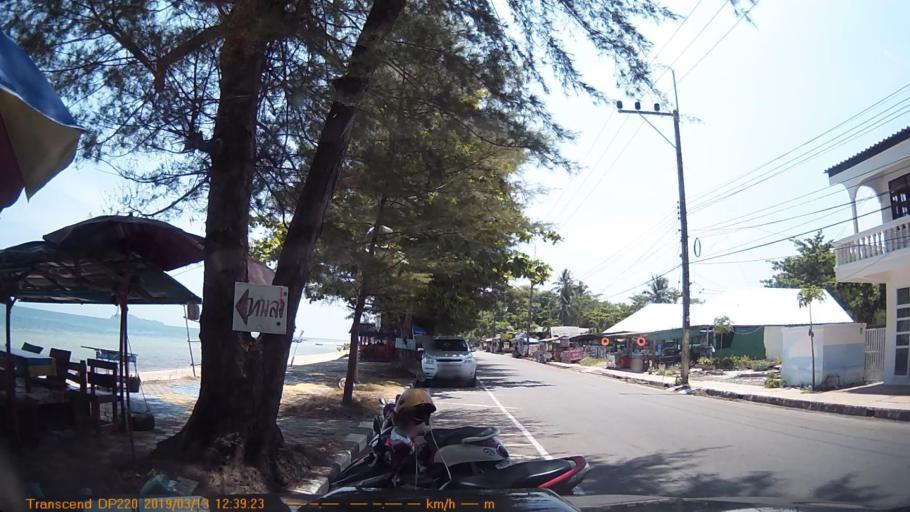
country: TH
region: Chumphon
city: Chumphon
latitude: 10.3970
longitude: 99.2796
